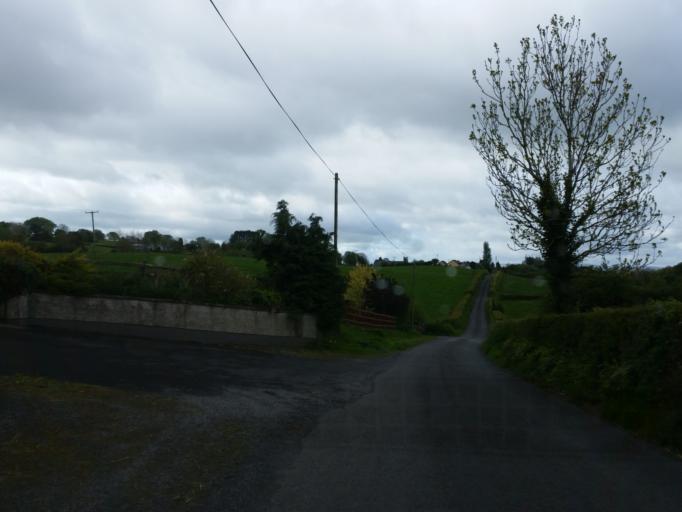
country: GB
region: Northern Ireland
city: Lisnaskea
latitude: 54.3243
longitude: -7.3932
